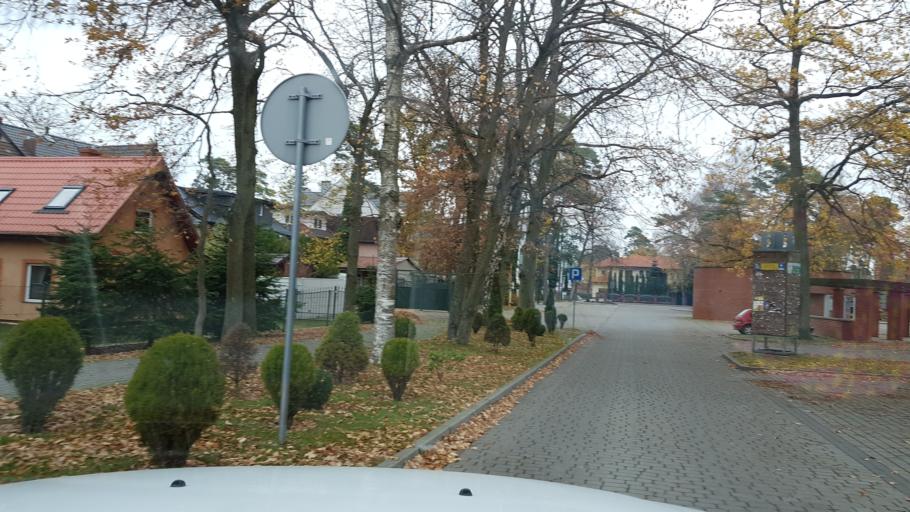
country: PL
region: West Pomeranian Voivodeship
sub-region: Powiat gryficki
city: Pobierowo
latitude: 54.0599
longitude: 14.9330
